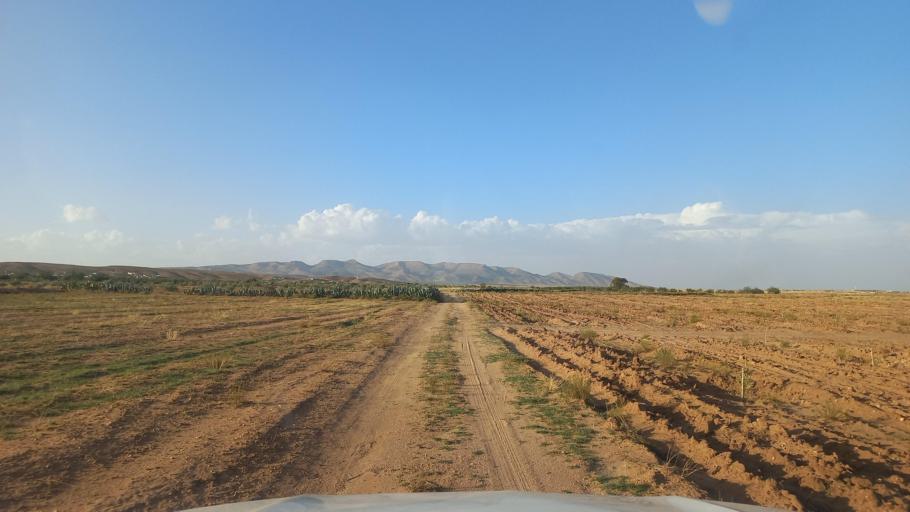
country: TN
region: Al Qasrayn
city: Sbiba
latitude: 35.3630
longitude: 9.0210
